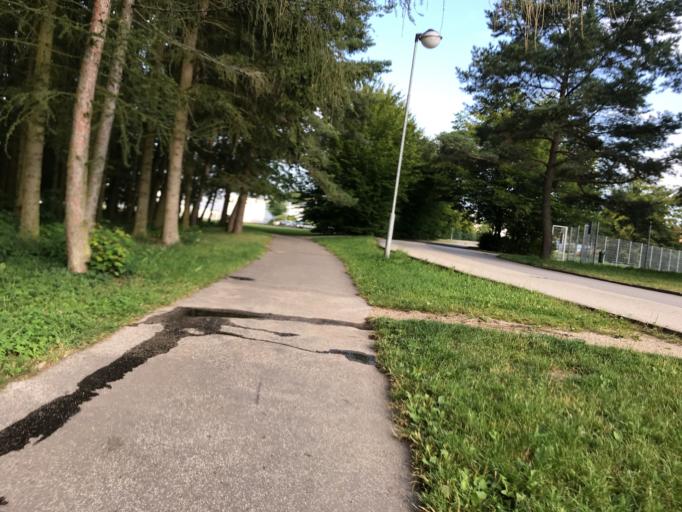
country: CZ
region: Jihocesky
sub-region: Okres Jindrichuv Hradec
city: Trebon
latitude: 49.0015
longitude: 14.7559
